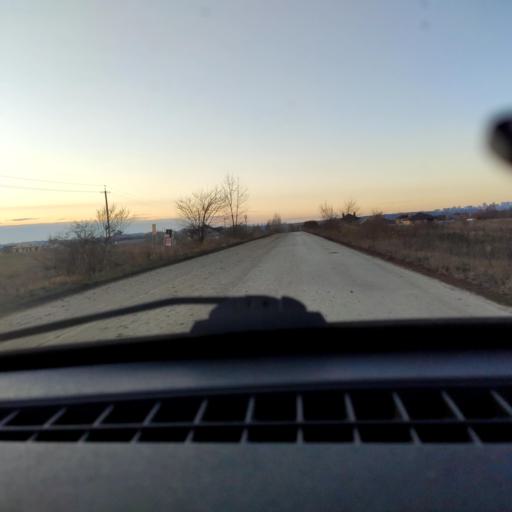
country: RU
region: Bashkortostan
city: Ufa
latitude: 54.7043
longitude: 56.1145
